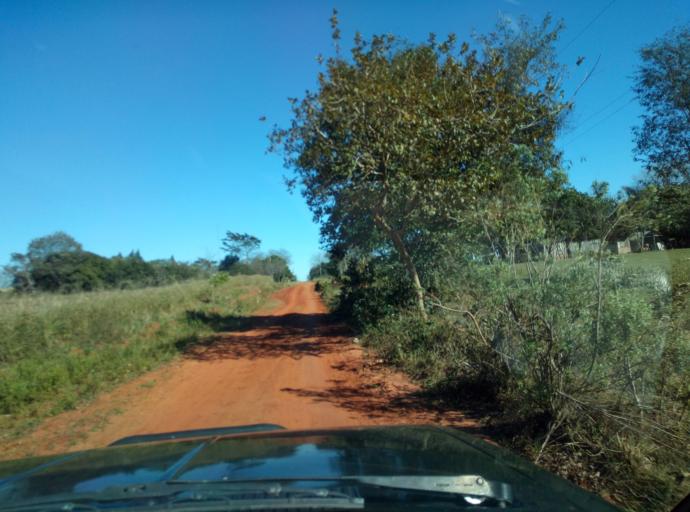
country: PY
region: Caaguazu
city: Doctor Cecilio Baez
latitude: -25.1790
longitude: -56.2404
